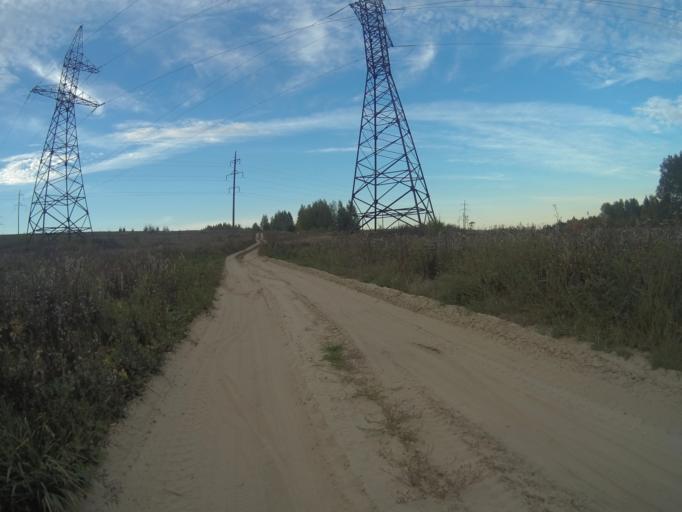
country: RU
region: Vladimir
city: Raduzhnyy
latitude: 55.9962
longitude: 40.3718
